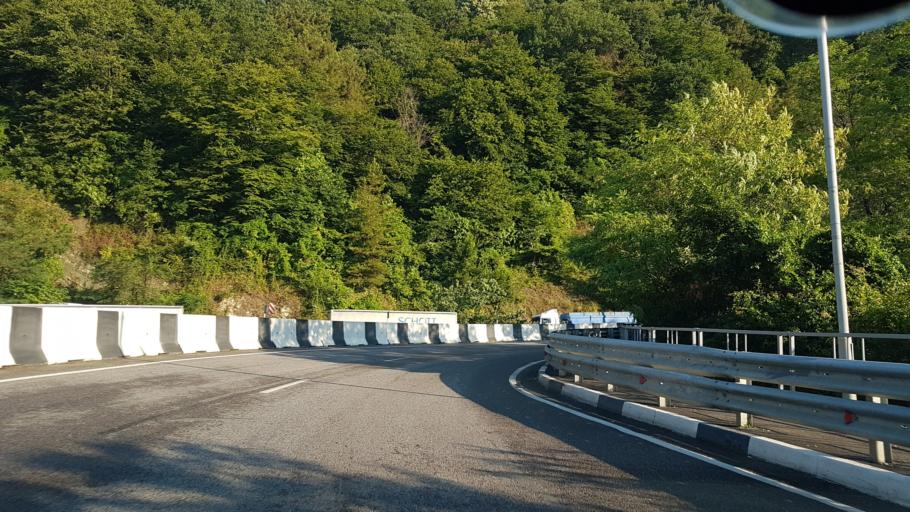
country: RU
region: Krasnodarskiy
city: Dagomys
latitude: 43.6395
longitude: 39.6983
